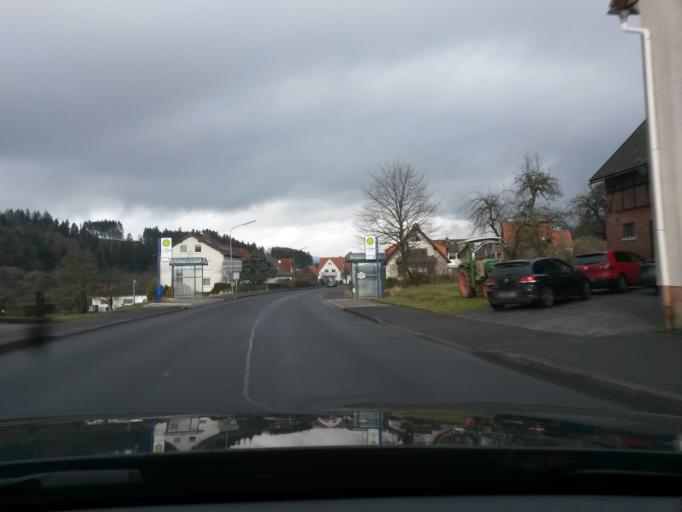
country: DE
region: Thuringia
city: Birx
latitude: 50.5277
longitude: 10.0137
